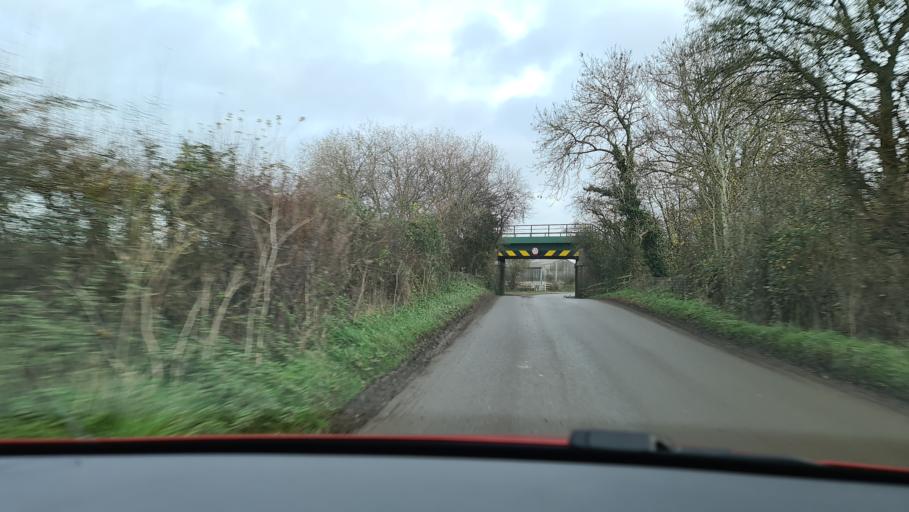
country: GB
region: England
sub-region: Buckinghamshire
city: Long Crendon
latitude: 51.7968
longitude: -0.9805
